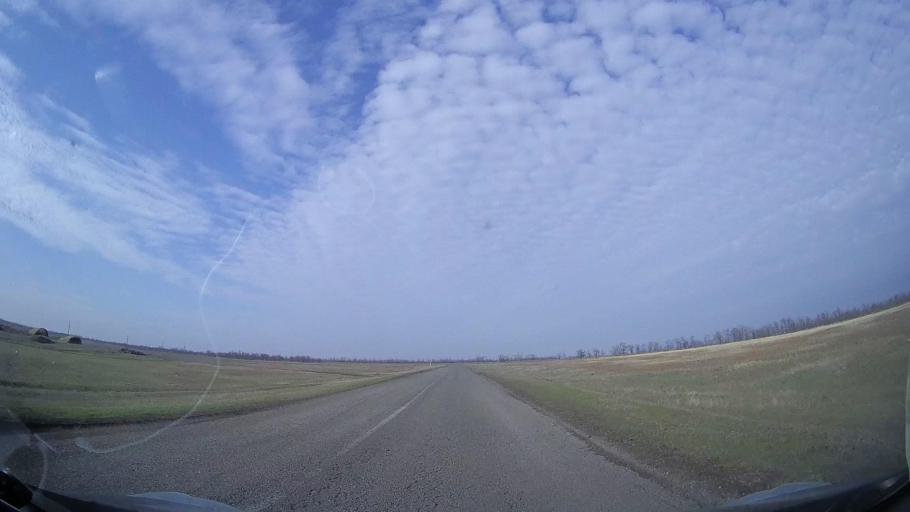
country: RU
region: Rostov
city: Gigant
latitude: 46.8487
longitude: 41.3230
